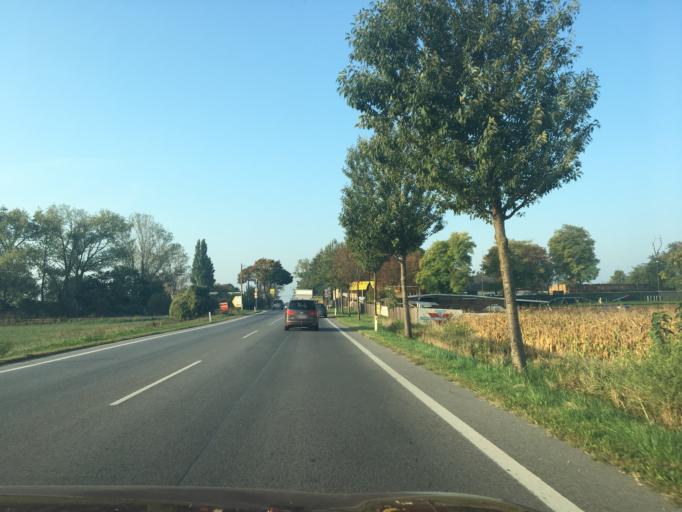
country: AT
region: Lower Austria
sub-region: Politischer Bezirk Korneuburg
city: Hagenbrunn
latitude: 48.3131
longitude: 16.4317
